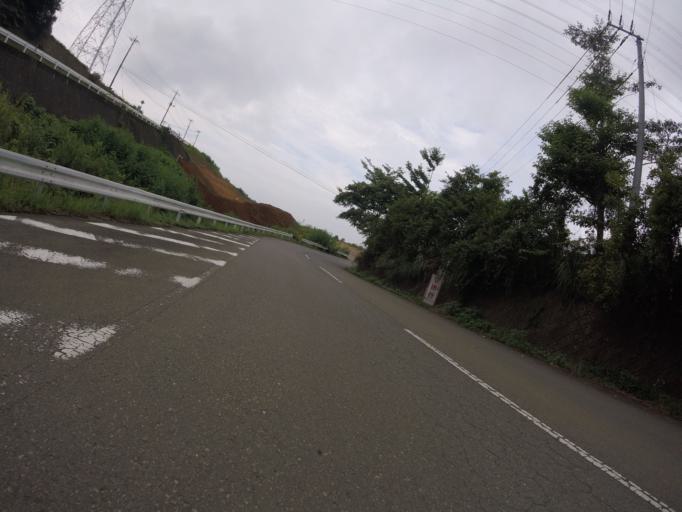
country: JP
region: Shizuoka
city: Mishima
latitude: 35.1400
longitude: 138.9767
